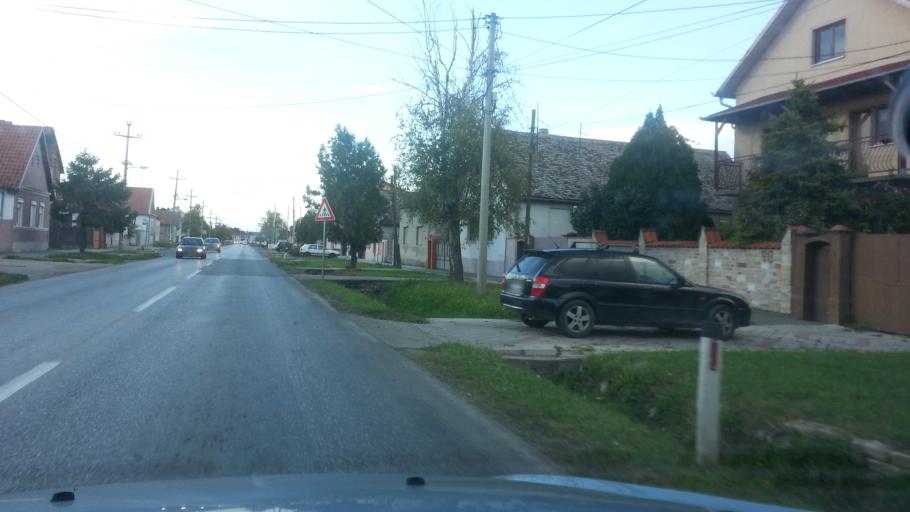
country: RS
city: Novi Banovci
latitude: 44.9100
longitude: 20.2681
